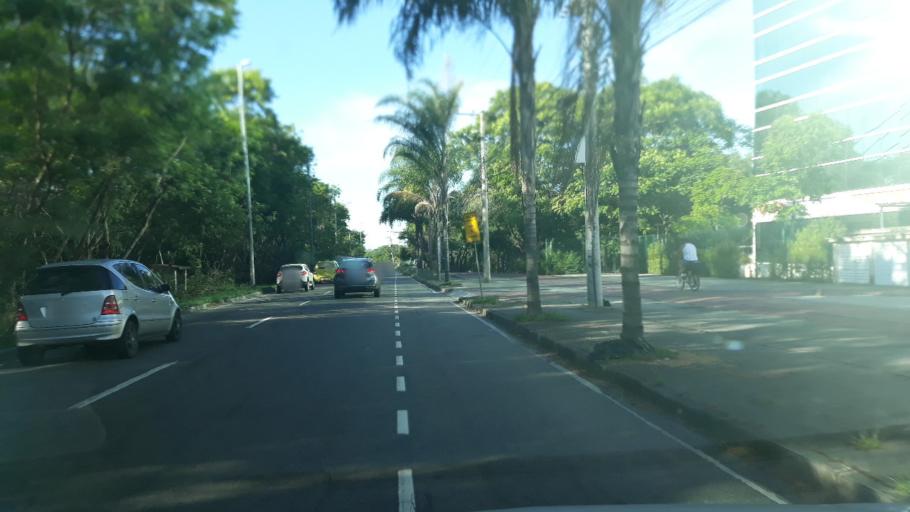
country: BR
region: Rio de Janeiro
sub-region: Sao Joao De Meriti
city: Sao Joao de Meriti
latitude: -22.9749
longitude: -43.3646
